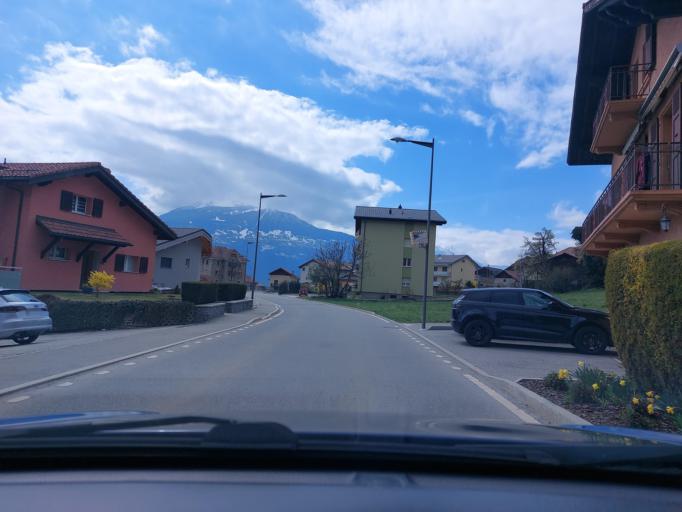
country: CH
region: Valais
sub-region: Conthey District
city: Conthey
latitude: 46.2424
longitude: 7.2960
